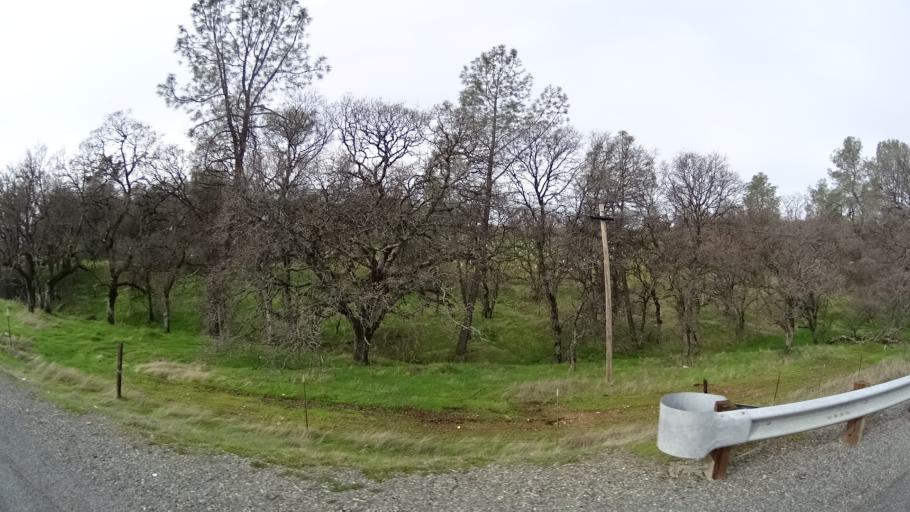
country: US
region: California
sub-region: Yuba County
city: Loma Rica
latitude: 39.4002
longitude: -121.4151
